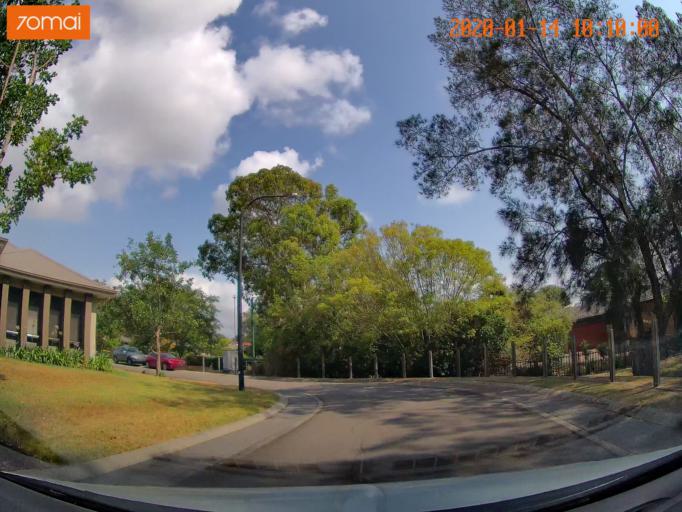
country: AU
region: New South Wales
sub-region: Wyong Shire
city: Kingfisher Shores
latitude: -33.1229
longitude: 151.5376
